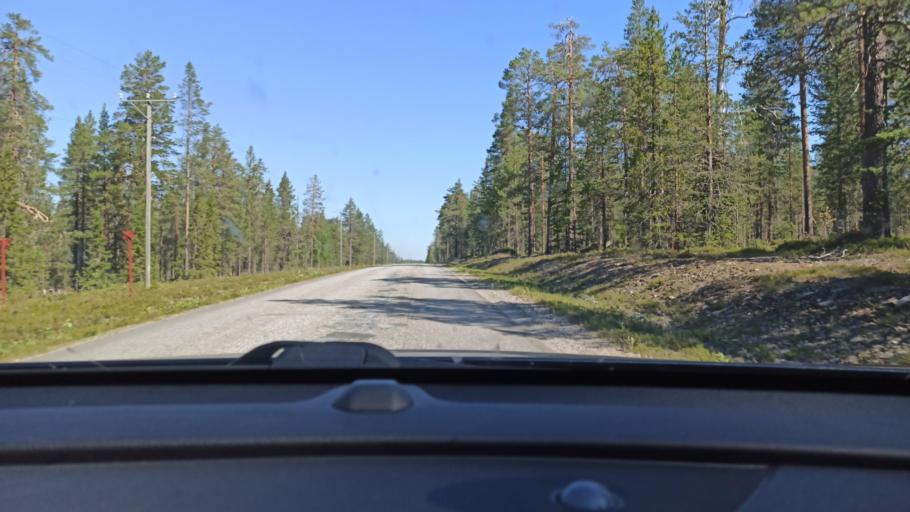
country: FI
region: Lapland
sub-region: Tunturi-Lappi
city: Kolari
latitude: 67.6400
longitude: 24.1575
